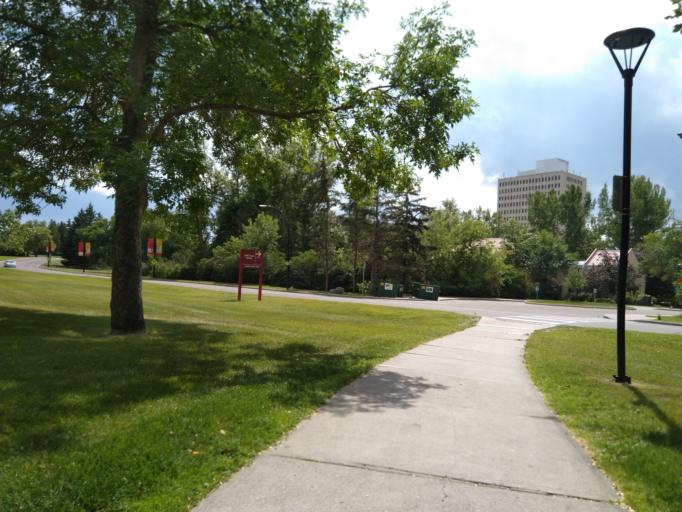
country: CA
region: Alberta
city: Calgary
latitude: 51.0792
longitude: -114.1241
